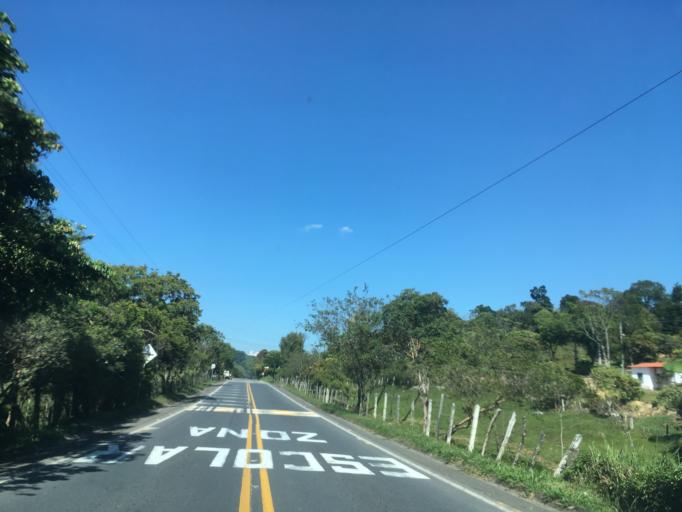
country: CO
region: Santander
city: Suaita
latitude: 6.0880
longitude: -73.3864
